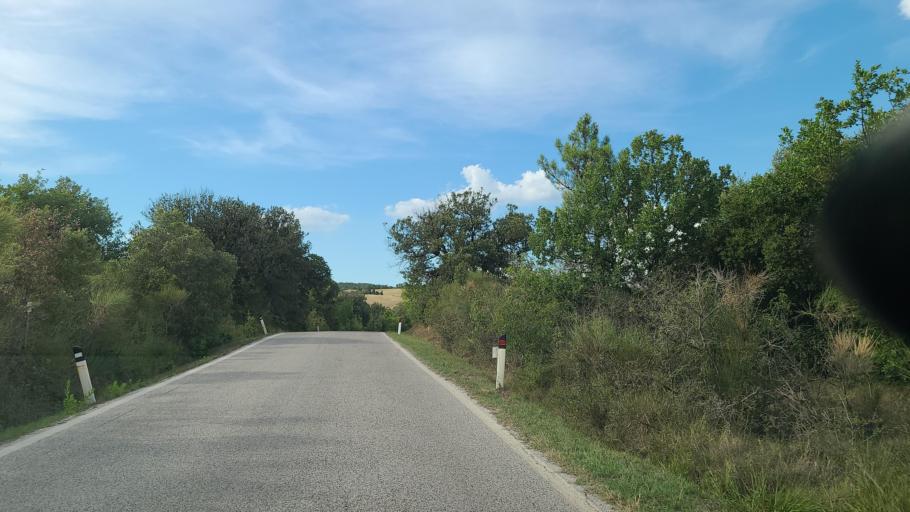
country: IT
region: Tuscany
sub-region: Provincia di Siena
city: San Gimignano
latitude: 43.4232
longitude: 10.9761
